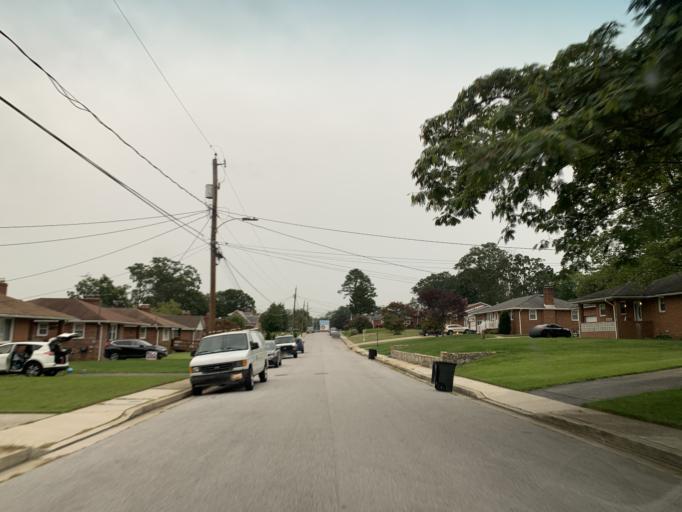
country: US
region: Maryland
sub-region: Baltimore County
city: Essex
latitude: 39.3203
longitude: -76.4780
